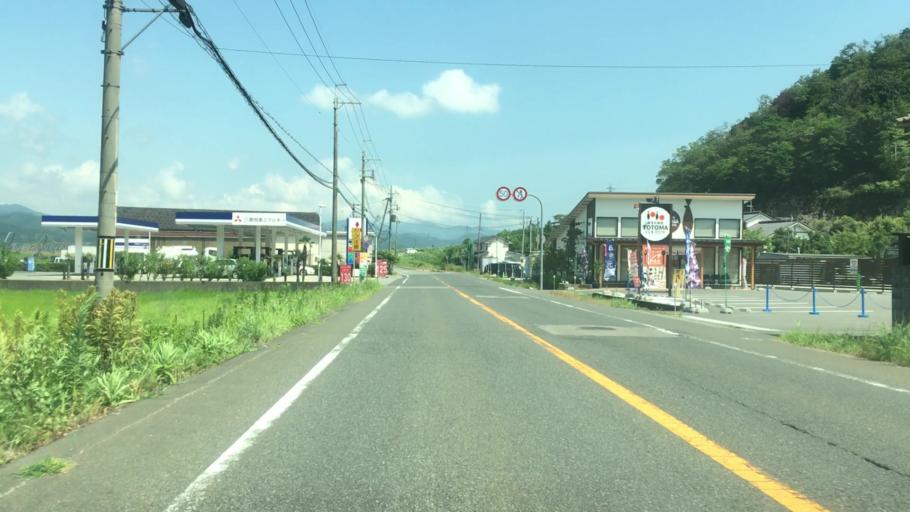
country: JP
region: Hyogo
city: Toyooka
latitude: 35.5650
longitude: 134.7925
